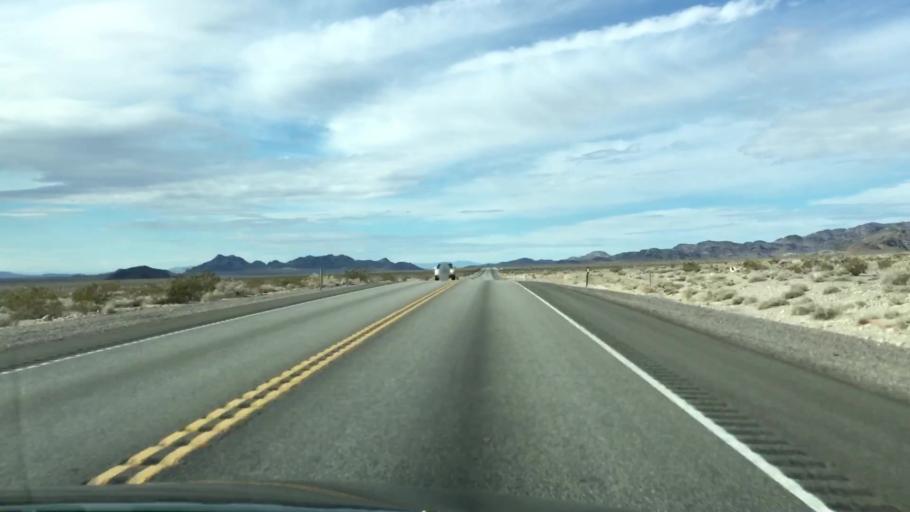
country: US
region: Nevada
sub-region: Nye County
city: Pahrump
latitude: 36.5869
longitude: -116.2161
